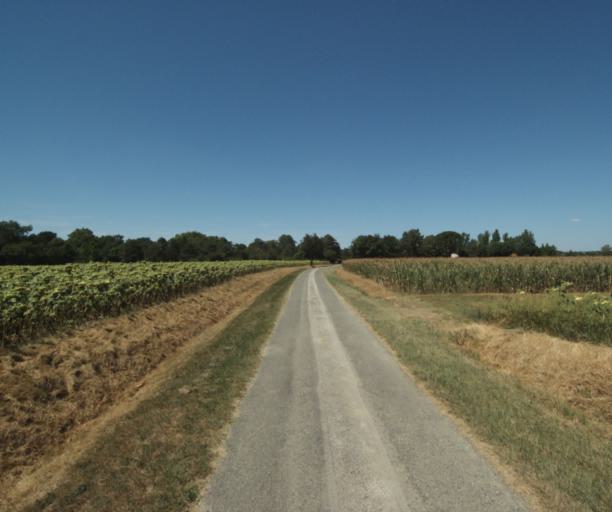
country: FR
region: Midi-Pyrenees
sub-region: Departement de la Haute-Garonne
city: Revel
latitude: 43.4775
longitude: 1.9470
